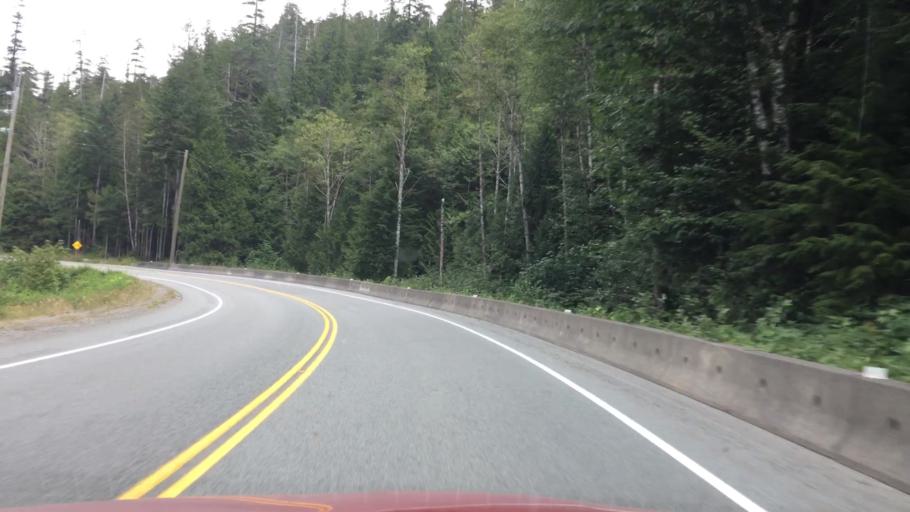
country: CA
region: British Columbia
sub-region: Regional District of Alberni-Clayoquot
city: Ucluelet
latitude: 49.2045
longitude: -125.3755
